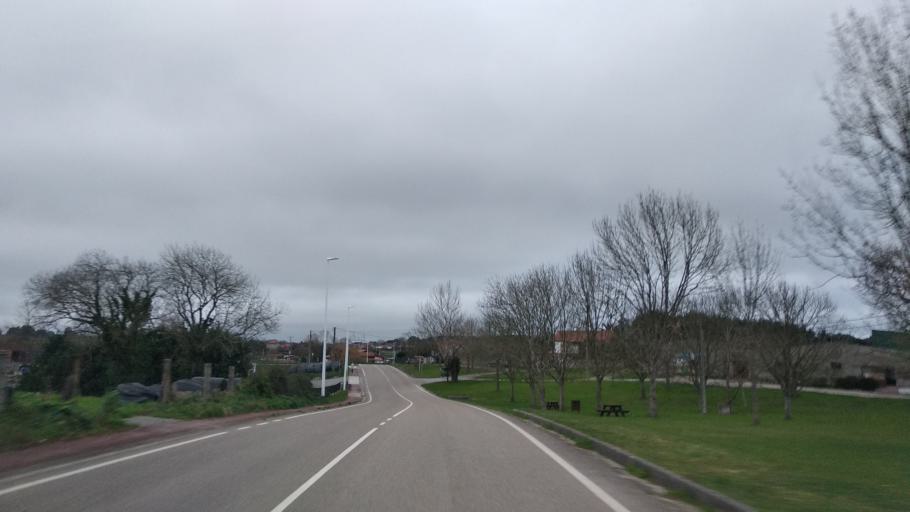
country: ES
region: Cantabria
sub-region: Provincia de Cantabria
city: Entrambasaguas
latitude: 43.4451
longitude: -3.7234
